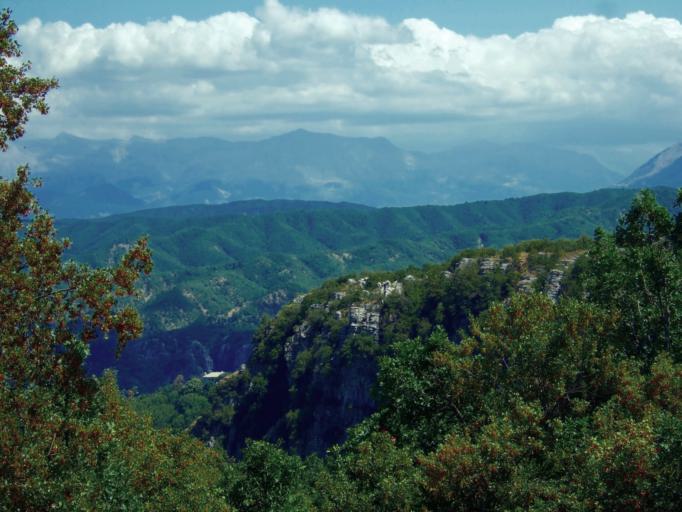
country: GR
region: Epirus
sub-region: Nomos Ioanninon
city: Asprangeloi
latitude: 39.8811
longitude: 20.7435
